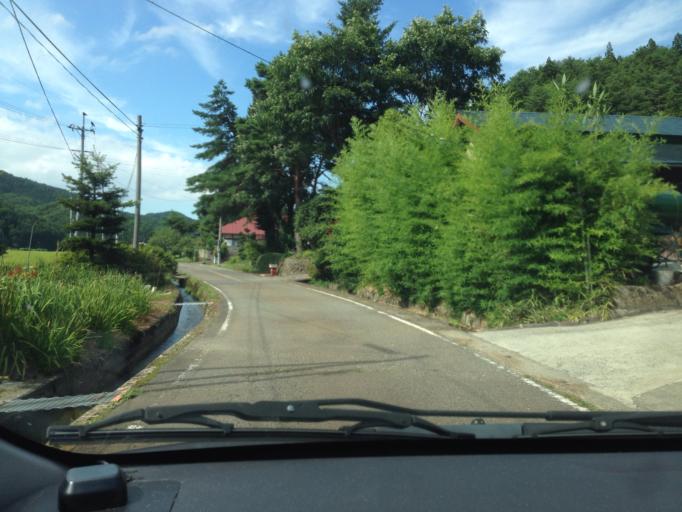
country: JP
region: Fukushima
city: Inawashiro
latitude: 37.3660
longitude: 140.0832
